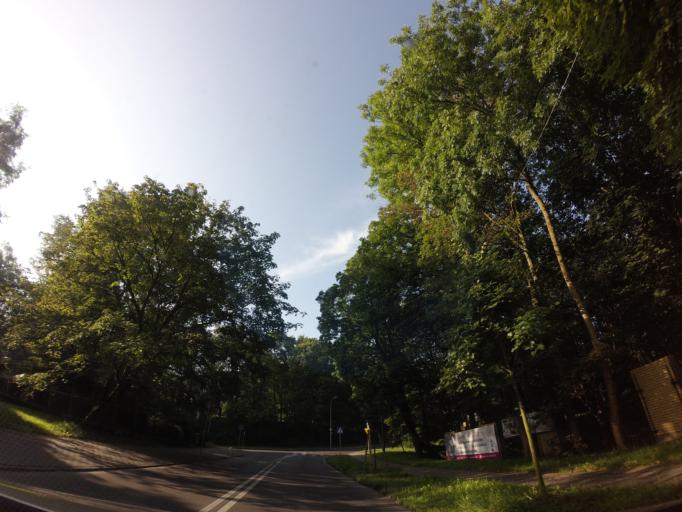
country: PL
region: West Pomeranian Voivodeship
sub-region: Szczecin
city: Szczecin
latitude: 53.4471
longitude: 14.5276
